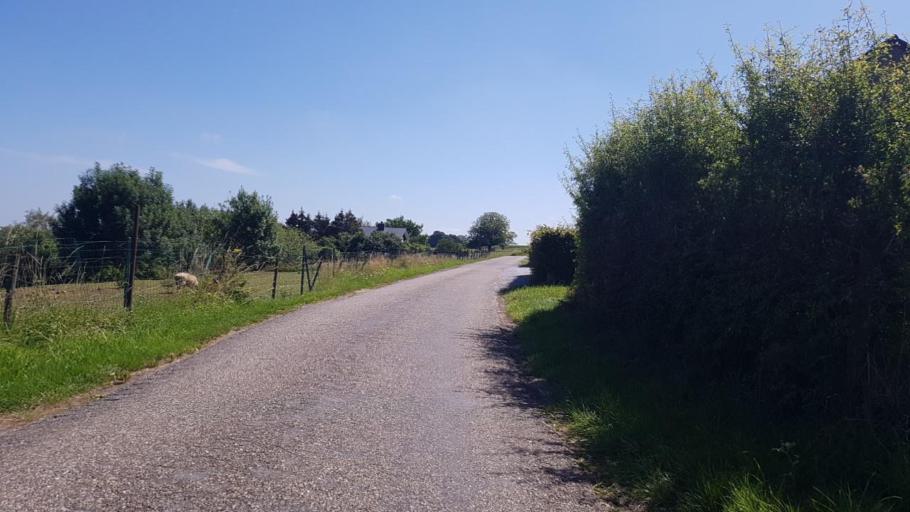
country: BE
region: Wallonia
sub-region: Province du Hainaut
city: Chimay
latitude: 50.0654
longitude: 4.2408
